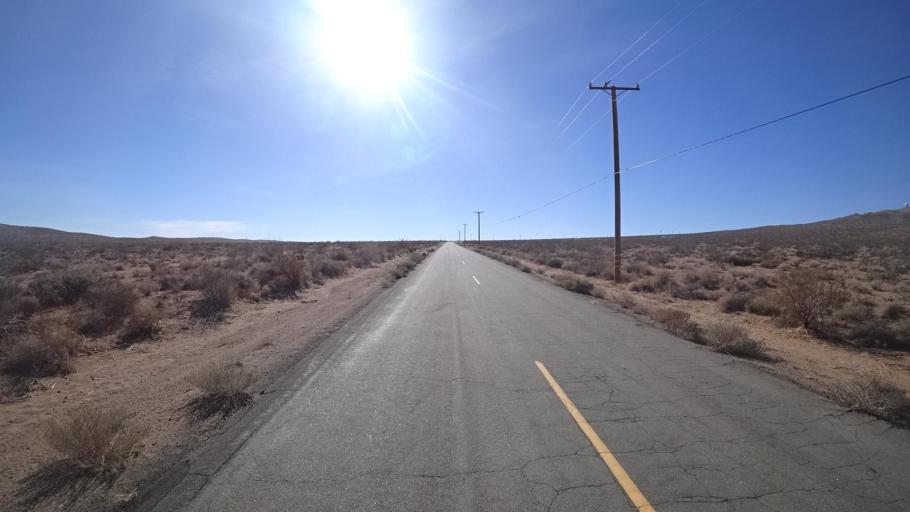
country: US
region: California
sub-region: Kern County
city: Ridgecrest
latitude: 35.4772
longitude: -117.6479
